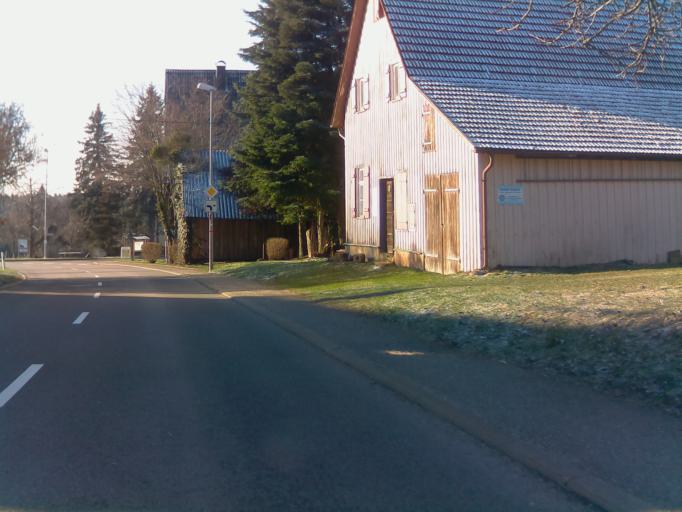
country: DE
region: Baden-Wuerttemberg
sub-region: Karlsruhe Region
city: Neuweiler
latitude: 48.6964
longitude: 8.5914
